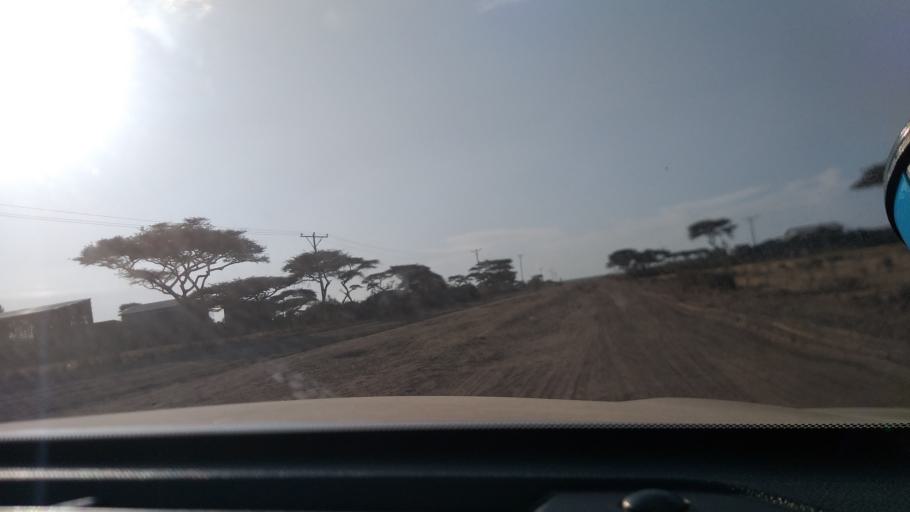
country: ET
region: Oromiya
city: Shashemene
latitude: 7.4975
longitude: 38.7007
